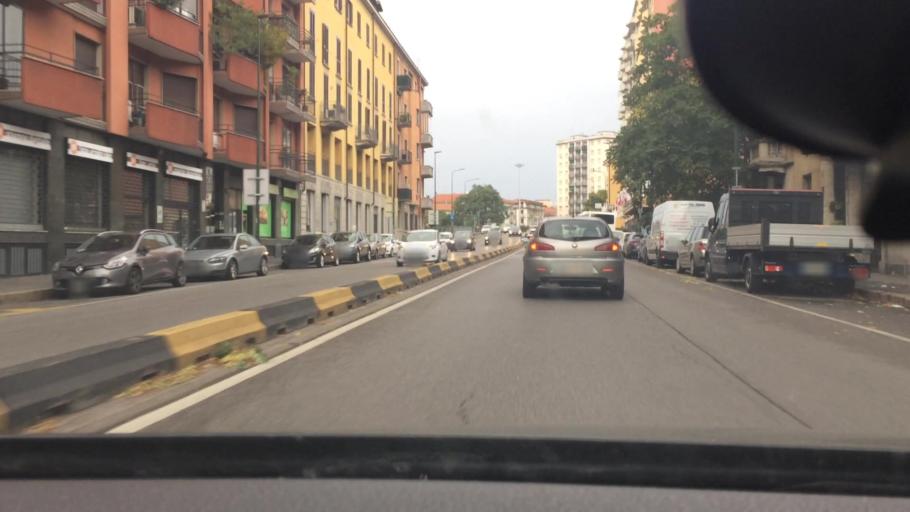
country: IT
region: Lombardy
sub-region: Citta metropolitana di Milano
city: Sesto San Giovanni
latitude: 45.5288
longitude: 9.2290
